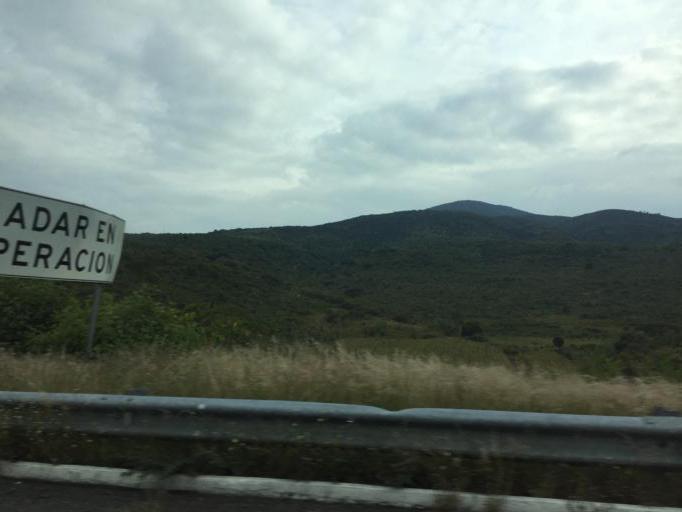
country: MX
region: Michoacan
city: Panindicuaro de la Reforma
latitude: 19.9729
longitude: -101.7283
